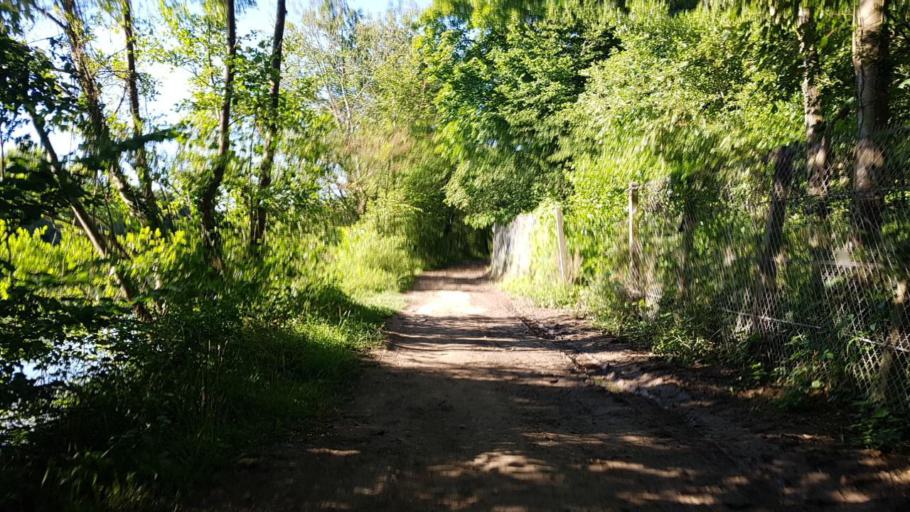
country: FR
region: Picardie
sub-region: Departement de l'Aisne
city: Essomes-sur-Marne
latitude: 49.0265
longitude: 3.3805
